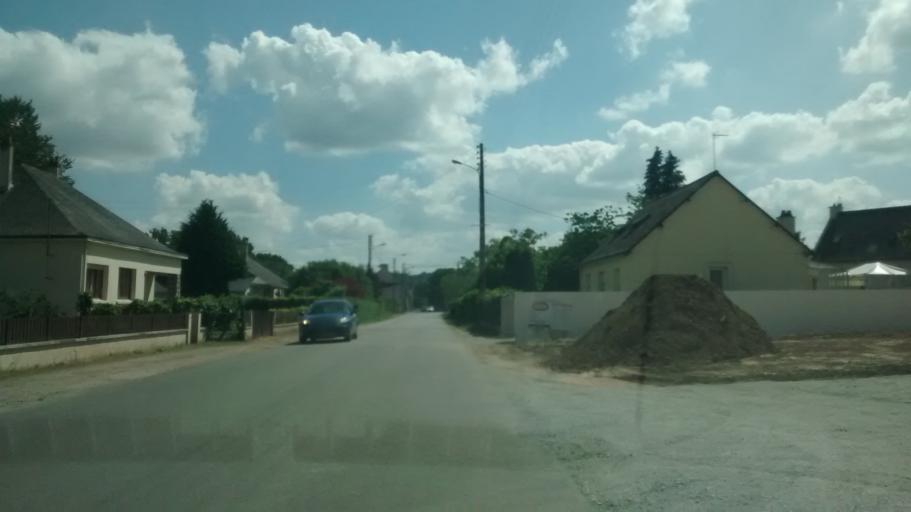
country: FR
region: Brittany
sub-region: Departement du Morbihan
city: Malestroit
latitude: 47.8168
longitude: -2.3742
